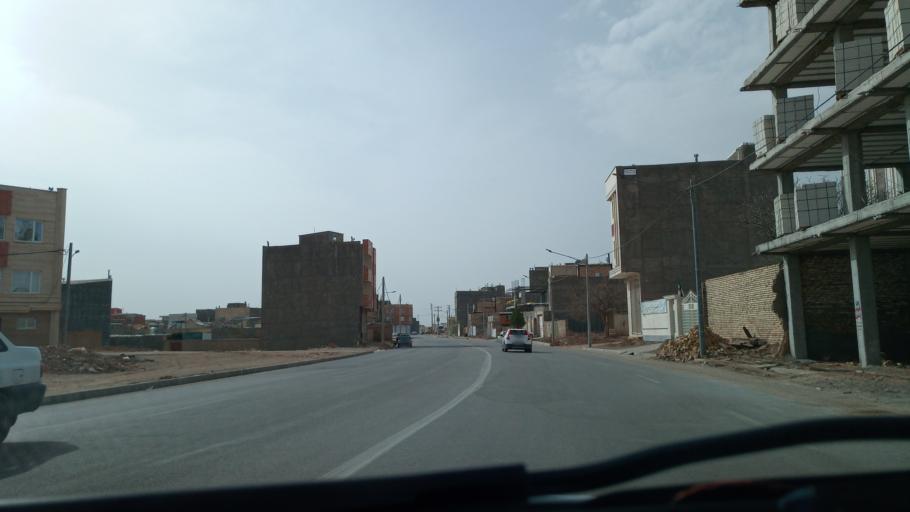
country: IR
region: Khorasan-e Shomali
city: Esfarayen
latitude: 37.0825
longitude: 57.5090
